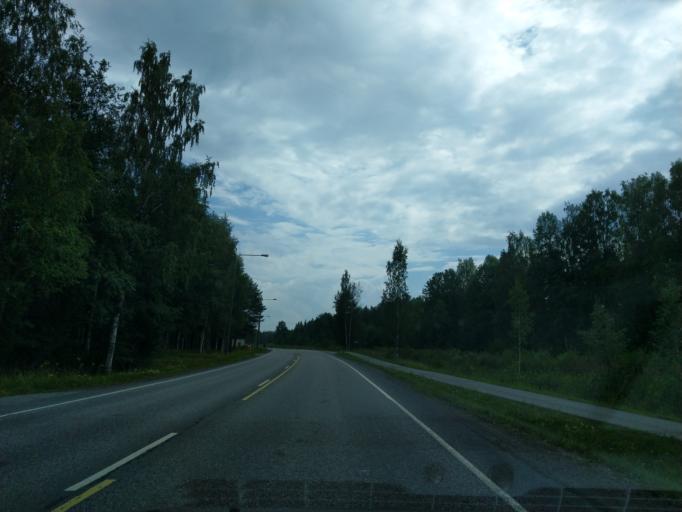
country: FI
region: South Karelia
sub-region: Imatra
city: Parikkala
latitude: 61.5954
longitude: 29.4846
